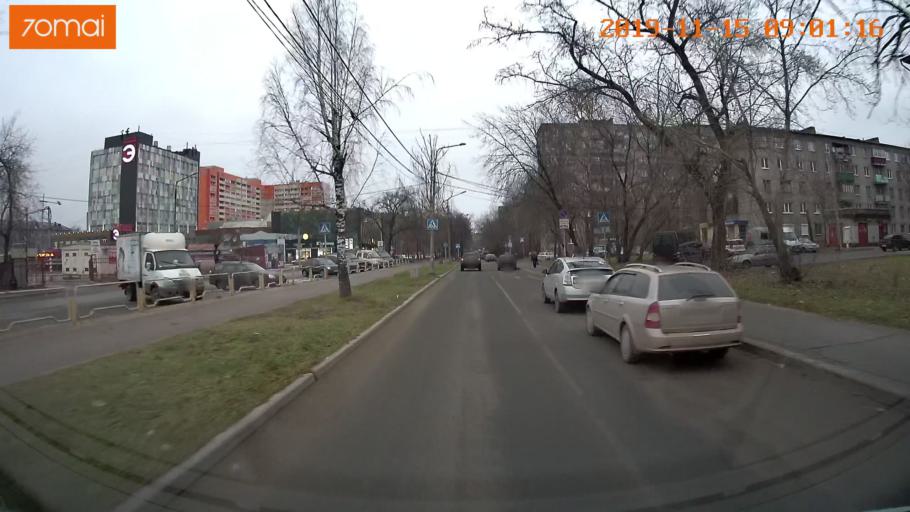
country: RU
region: Vologda
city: Cherepovets
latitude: 59.1314
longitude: 37.9255
